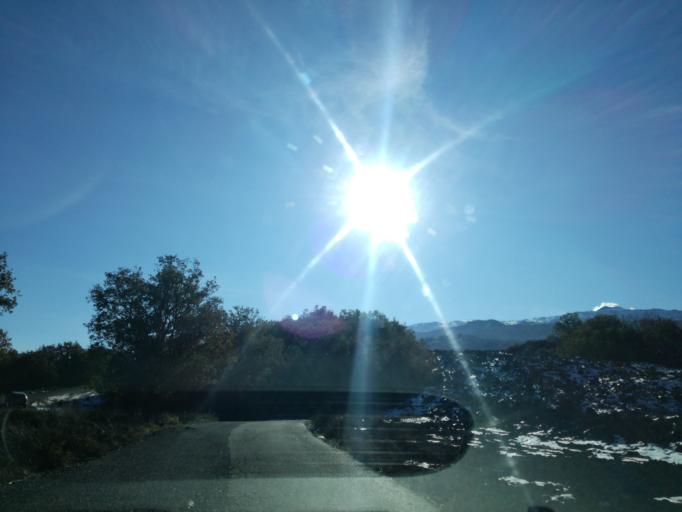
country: IT
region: Sicily
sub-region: Catania
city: Randazzo
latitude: 37.8595
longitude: 14.9804
